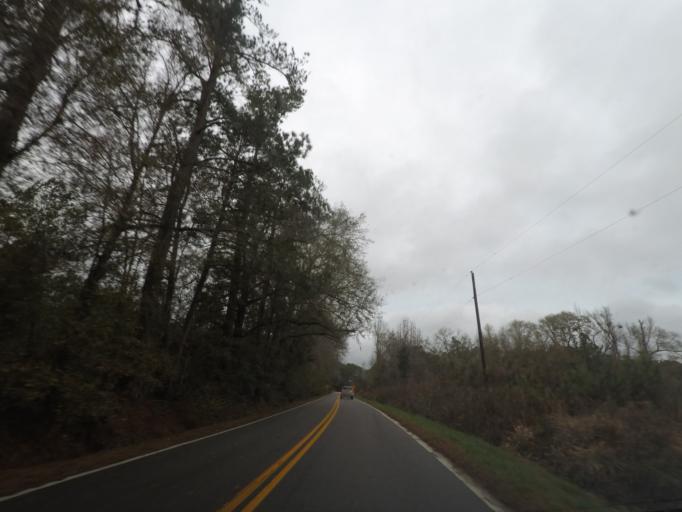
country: US
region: South Carolina
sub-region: Colleton County
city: Walterboro
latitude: 32.9350
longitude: -80.5392
